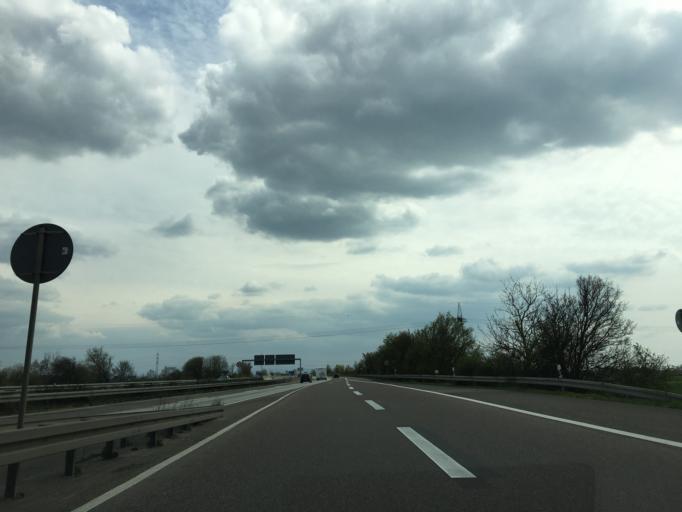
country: DE
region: Hesse
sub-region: Regierungsbezirk Darmstadt
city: Hochheim am Main
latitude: 50.0526
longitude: 8.3903
